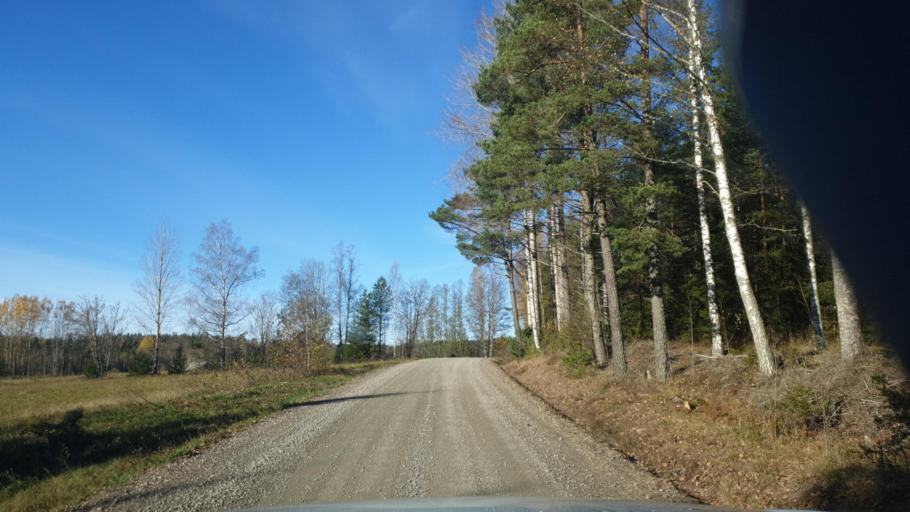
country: SE
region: Vaermland
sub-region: Karlstads Kommun
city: Edsvalla
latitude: 59.5094
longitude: 13.0211
